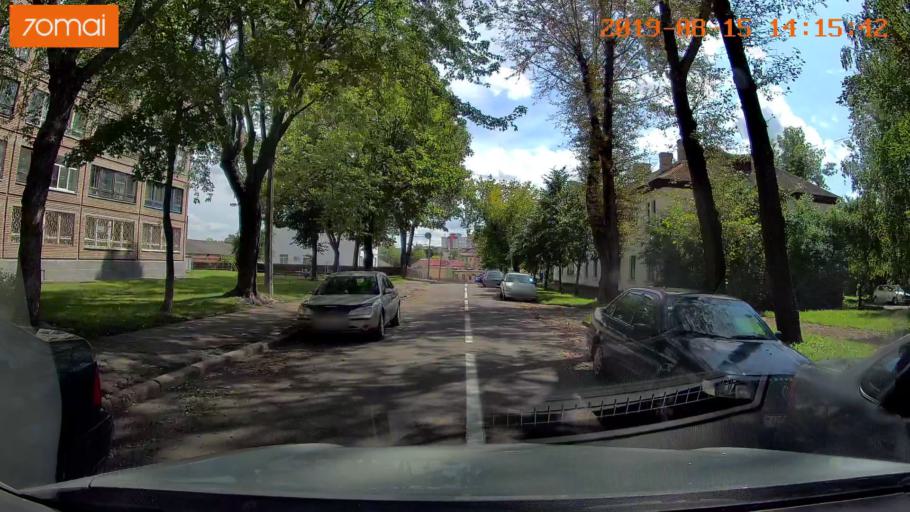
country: BY
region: Minsk
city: Minsk
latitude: 53.8878
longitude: 27.5918
